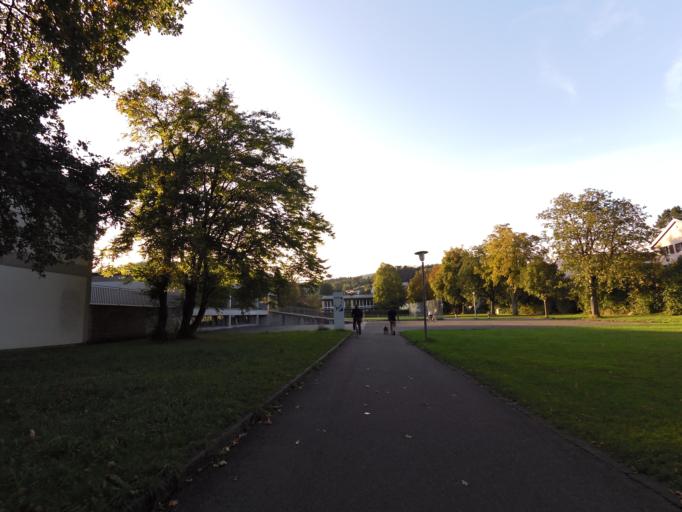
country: CH
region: Aargau
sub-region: Bezirk Aarau
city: Aarau
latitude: 47.3980
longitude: 8.0472
